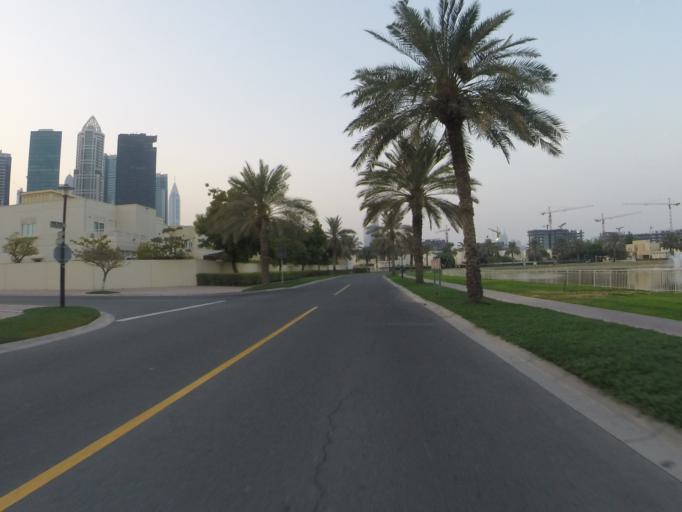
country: AE
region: Dubai
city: Dubai
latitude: 25.0737
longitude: 55.1556
